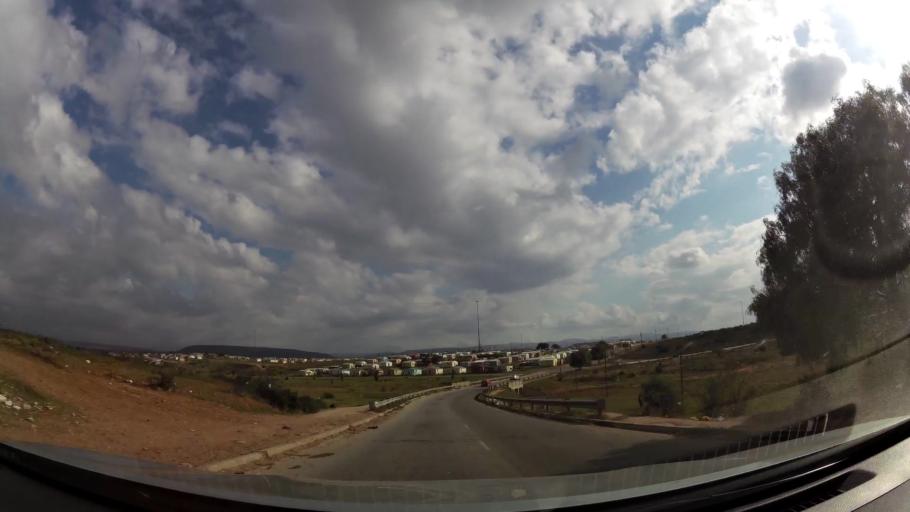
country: ZA
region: Eastern Cape
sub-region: Nelson Mandela Bay Metropolitan Municipality
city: Uitenhage
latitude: -33.7446
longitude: 25.3999
